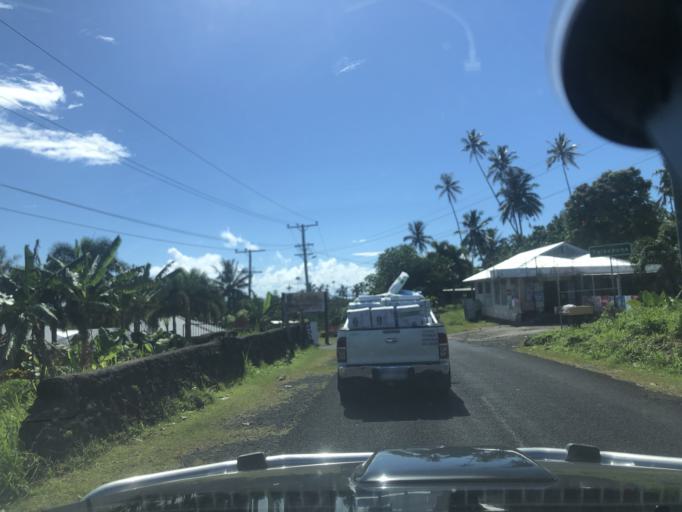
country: WS
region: Atua
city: Lufilufi
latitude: -13.8753
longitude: -171.5960
